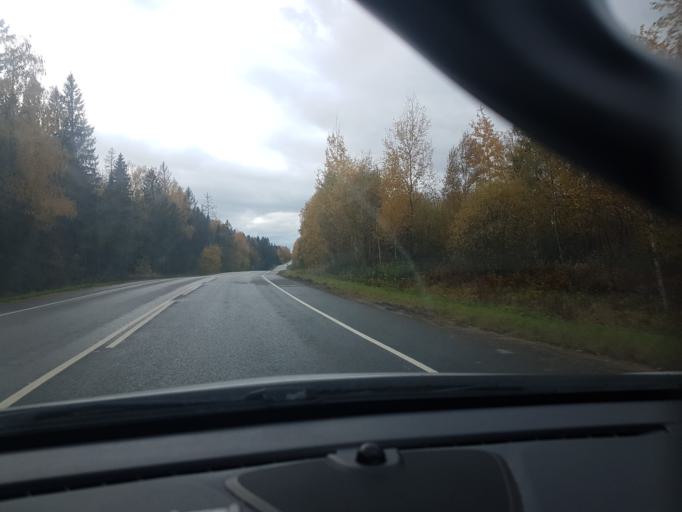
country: RU
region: Moskovskaya
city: Sychevo
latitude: 56.0043
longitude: 36.2970
